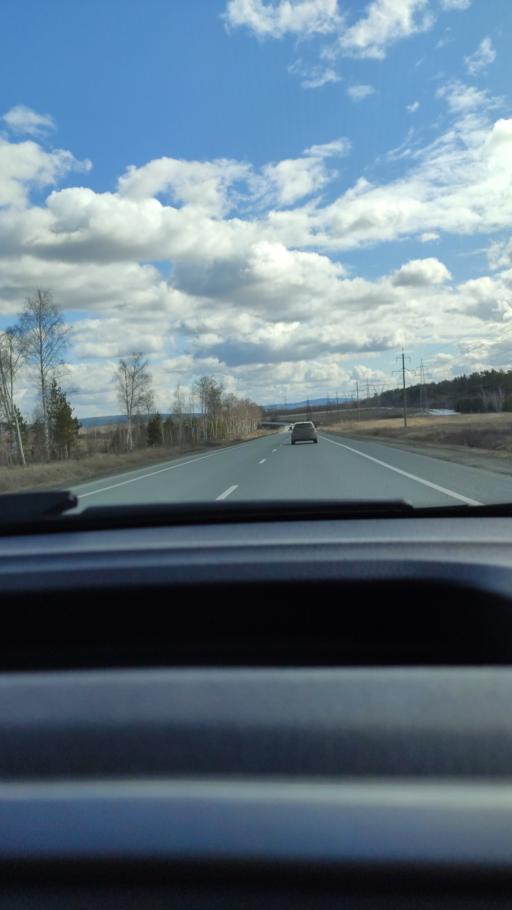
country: RU
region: Samara
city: Bogatyr'
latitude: 53.4951
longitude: 49.9640
